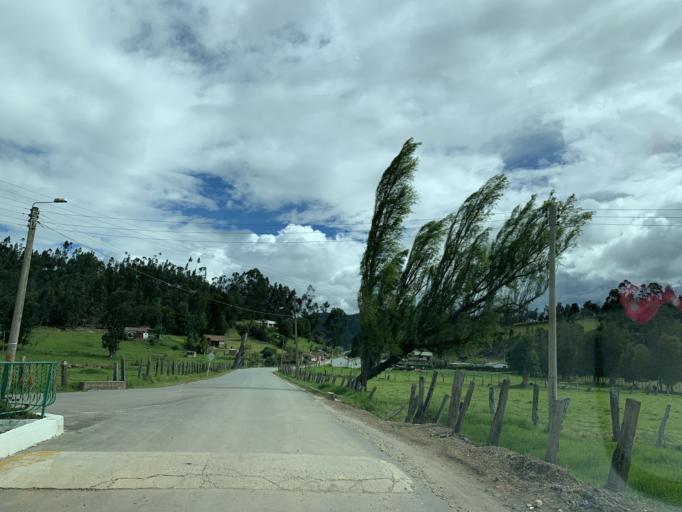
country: CO
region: Boyaca
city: Floresta
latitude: 5.8582
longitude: -72.9215
